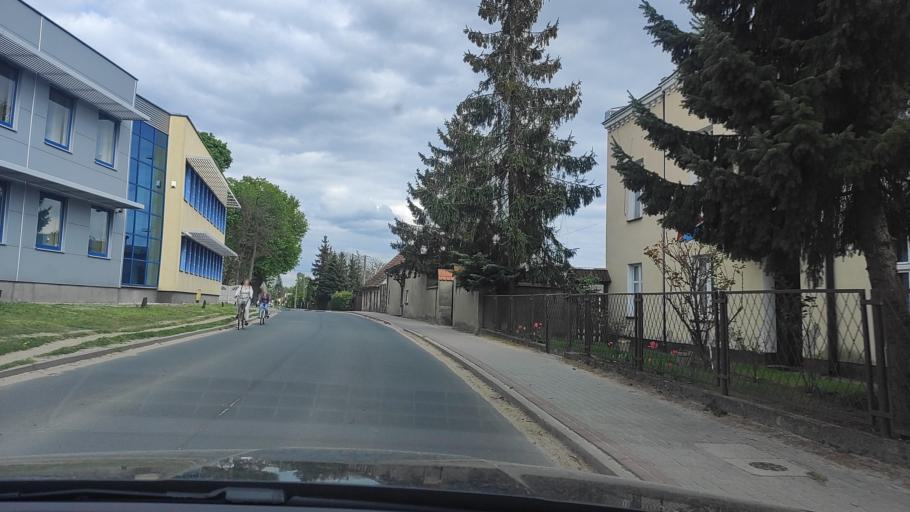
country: PL
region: Greater Poland Voivodeship
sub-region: Powiat poznanski
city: Kostrzyn
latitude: 52.4609
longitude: 17.1736
